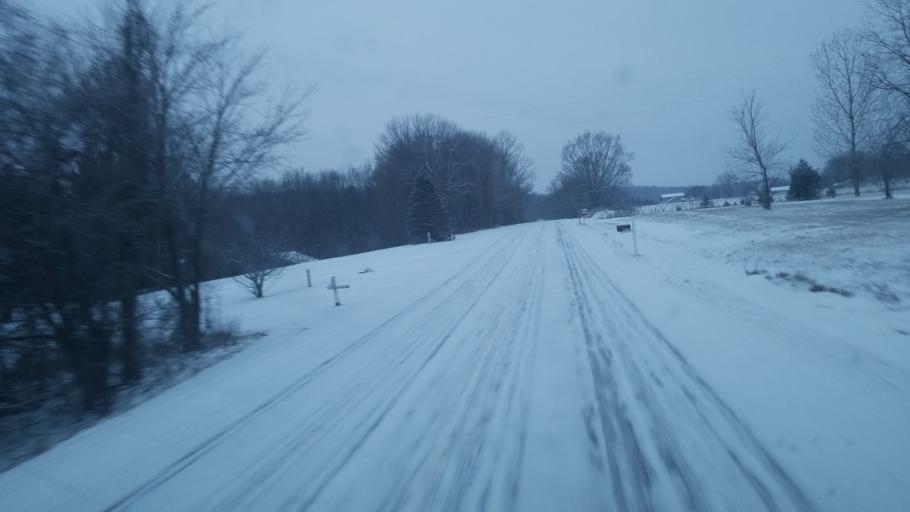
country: US
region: Michigan
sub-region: Osceola County
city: Reed City
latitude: 43.8219
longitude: -85.4180
